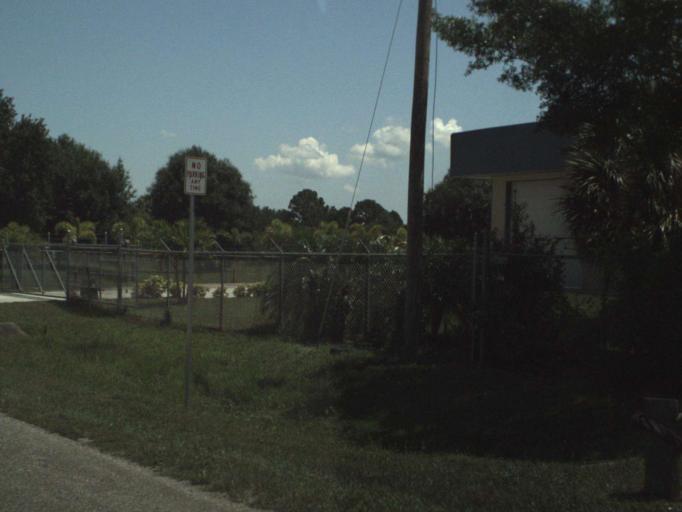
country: US
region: Florida
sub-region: Brevard County
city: Sharpes
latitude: 28.4313
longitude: -80.7079
